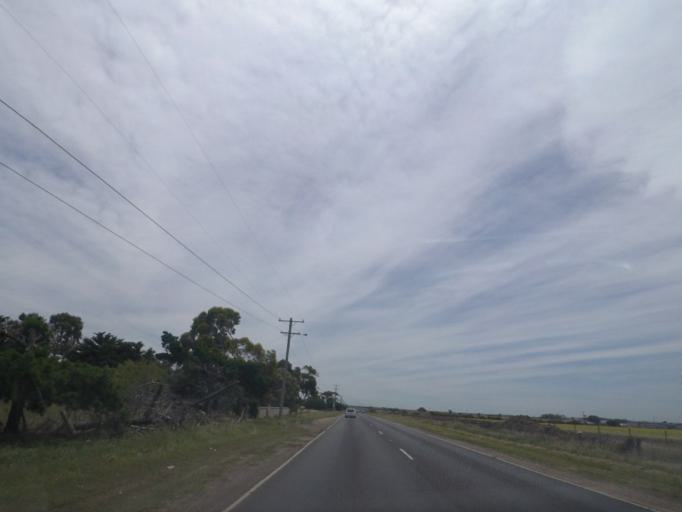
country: AU
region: Victoria
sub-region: Wyndham
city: Tarneit
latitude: -37.8267
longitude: 144.6924
